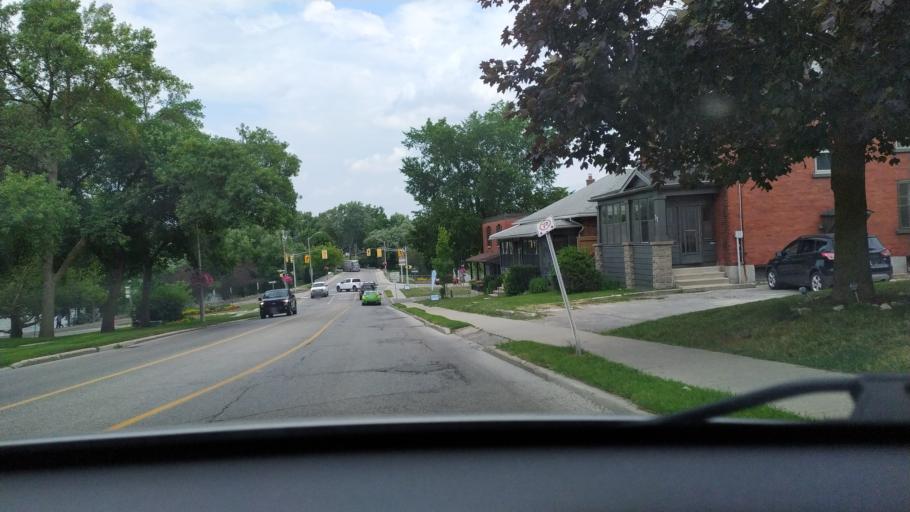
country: CA
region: Ontario
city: Stratford
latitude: 43.3724
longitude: -80.9797
